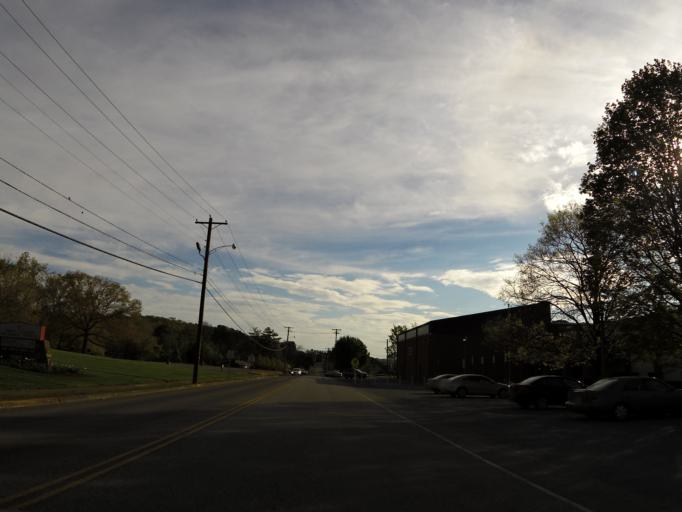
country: US
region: Tennessee
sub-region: Blount County
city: Maryville
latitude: 35.7417
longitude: -83.9702
